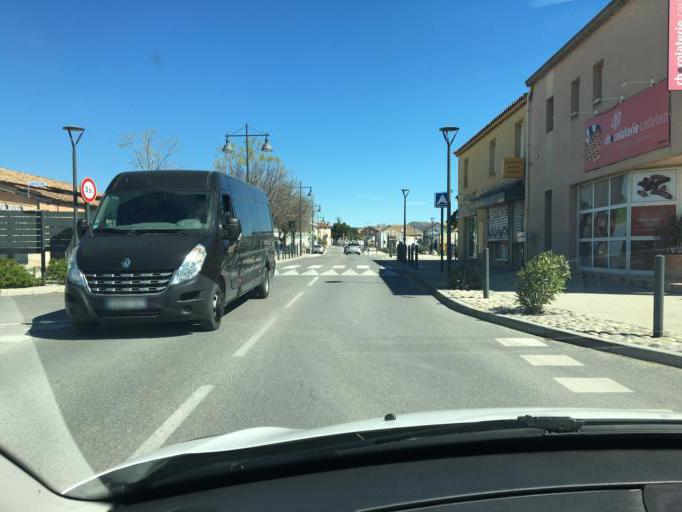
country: FR
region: Provence-Alpes-Cote d'Azur
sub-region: Departement du Vaucluse
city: Maubec
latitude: 43.8671
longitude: 5.1418
